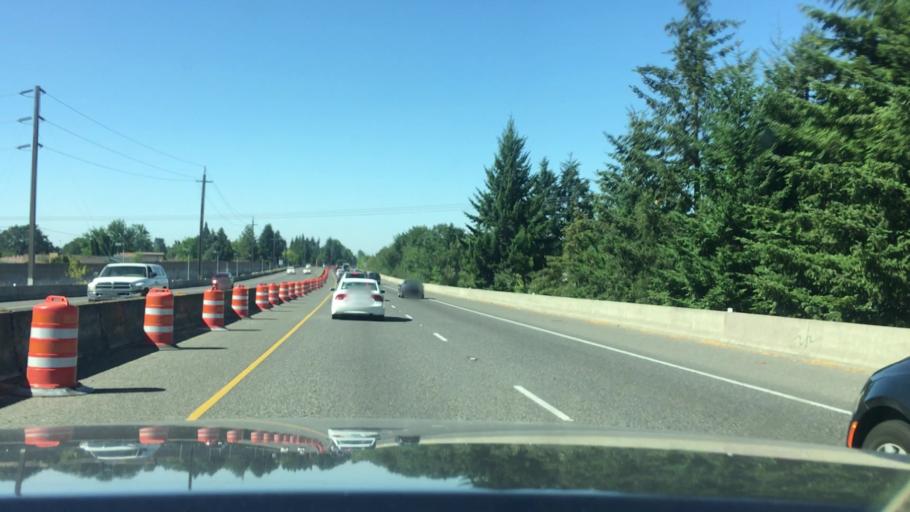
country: US
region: Oregon
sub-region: Lane County
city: Eugene
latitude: 44.0728
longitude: -123.1735
